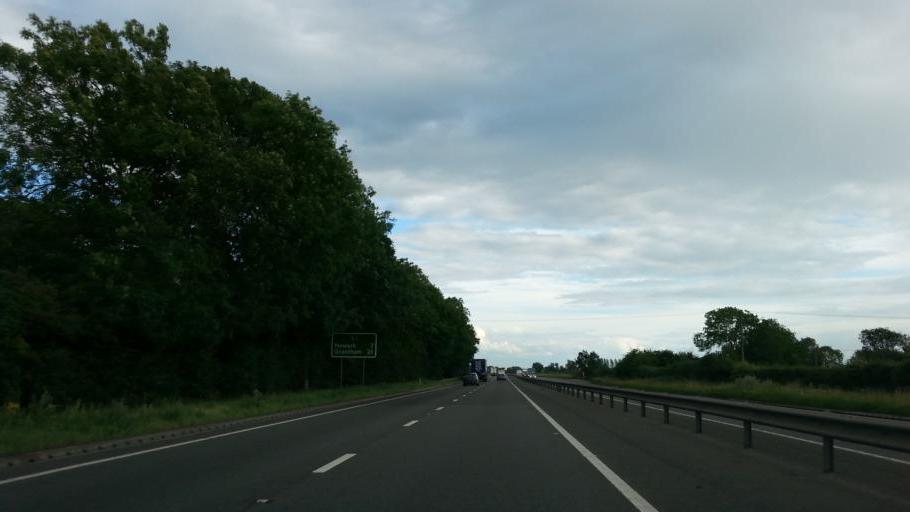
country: GB
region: England
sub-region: Nottinghamshire
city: South Collingham
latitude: 53.1622
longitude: -0.8082
